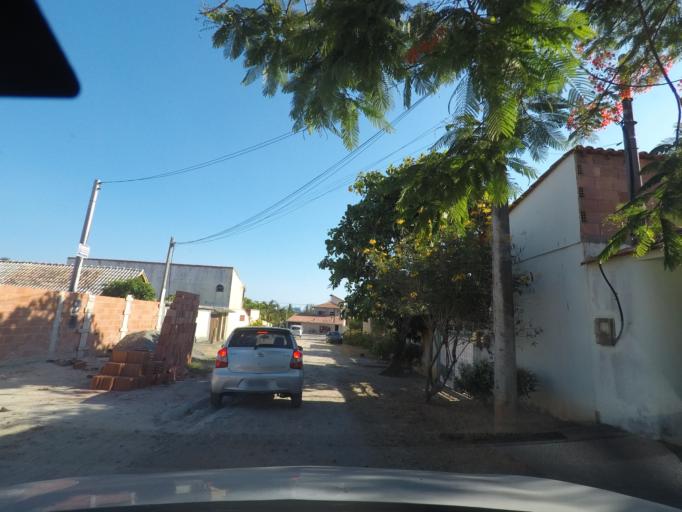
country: BR
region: Rio de Janeiro
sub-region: Marica
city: Marica
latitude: -22.9706
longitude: -42.9262
